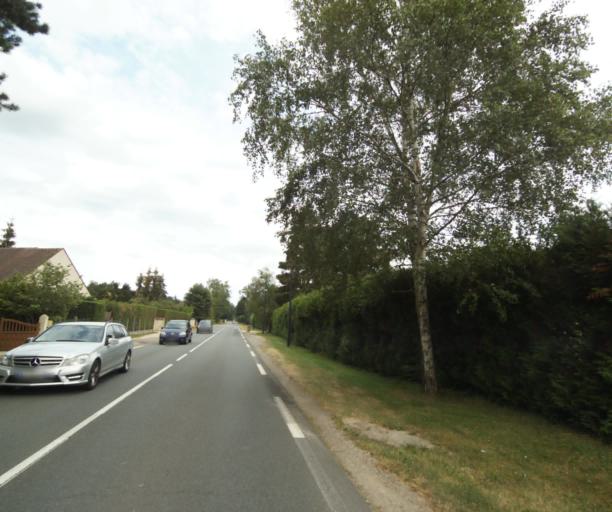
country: FR
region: Ile-de-France
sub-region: Departement de Seine-et-Marne
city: Arbonne-la-Foret
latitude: 48.4132
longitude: 2.5681
